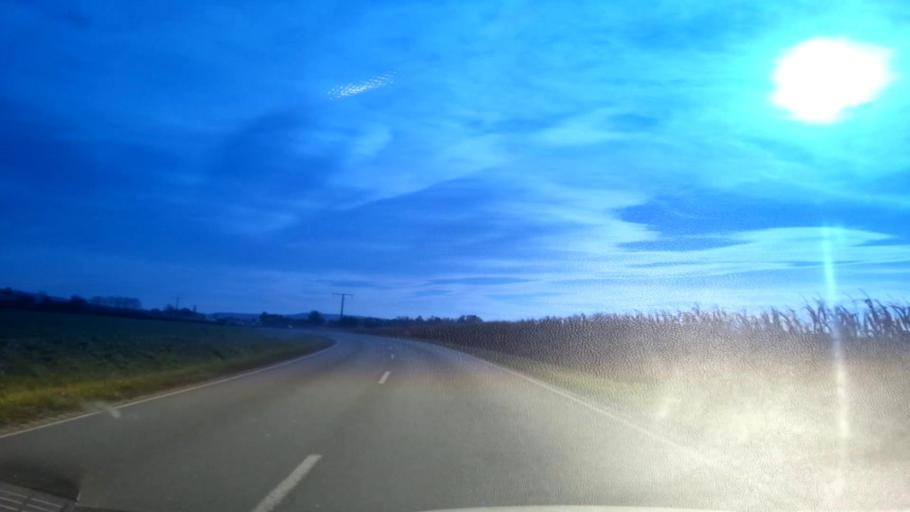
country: DE
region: Bavaria
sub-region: Upper Franconia
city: Reuth
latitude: 49.9530
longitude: 11.7063
